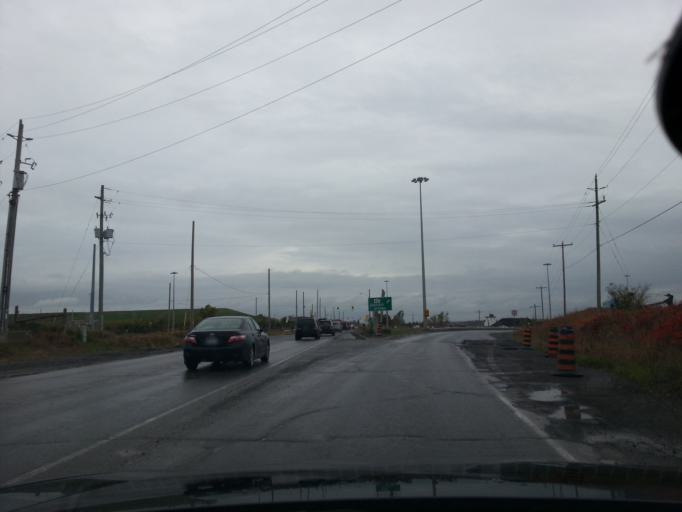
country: CA
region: Ontario
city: Bells Corners
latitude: 45.2793
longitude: -75.9547
